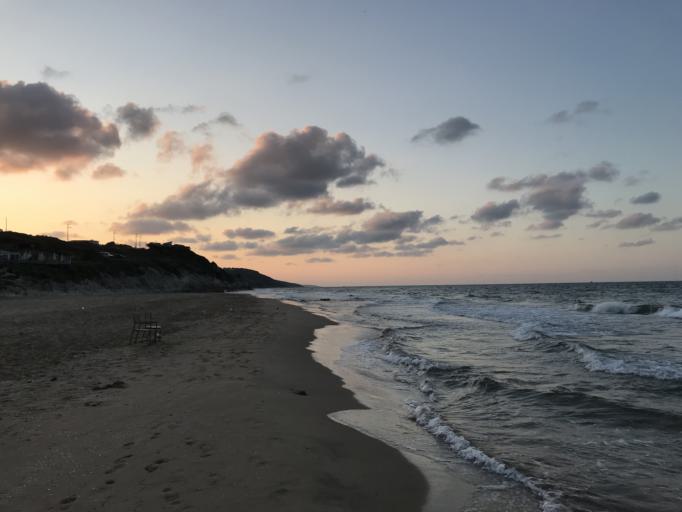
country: TR
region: Istanbul
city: Sile
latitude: 41.1727
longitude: 29.5722
